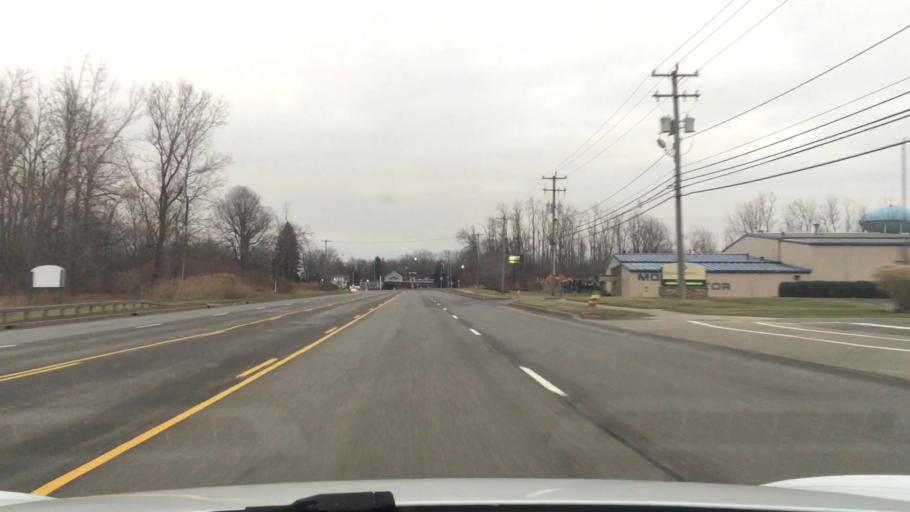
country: US
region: New York
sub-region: Erie County
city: Depew
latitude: 42.9370
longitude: -78.7020
